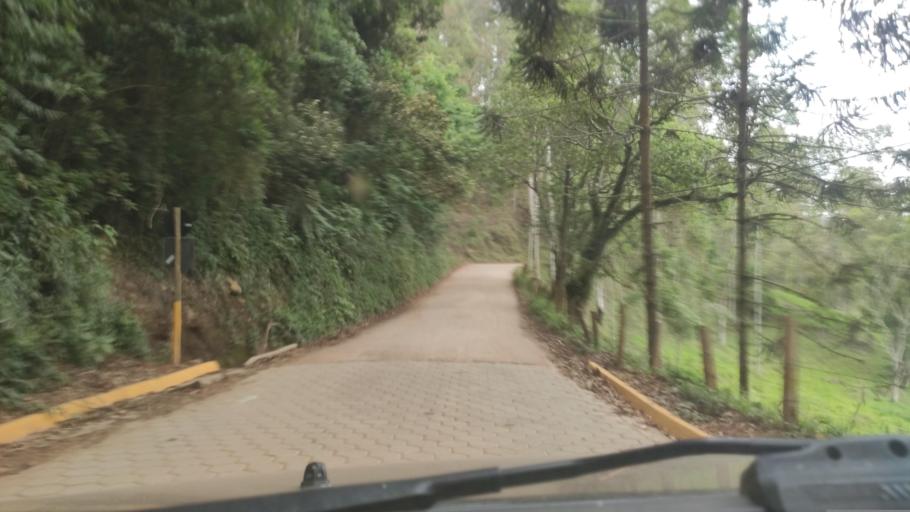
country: BR
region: Minas Gerais
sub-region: Paraisopolis
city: Paraisopolis
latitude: -22.6836
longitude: -45.8525
